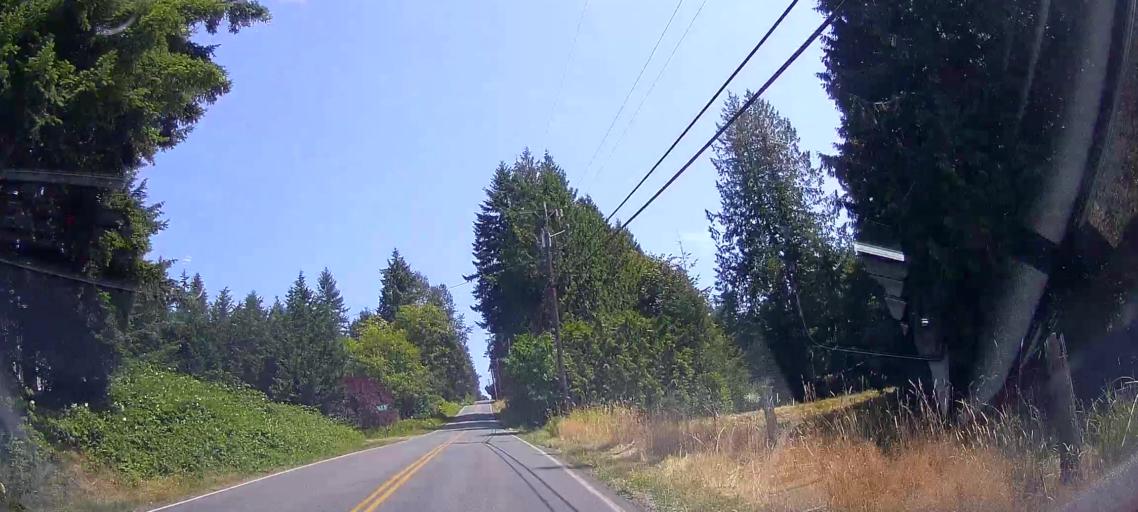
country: US
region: Washington
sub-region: Snohomish County
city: Sisco Heights
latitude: 48.0920
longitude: -122.1284
